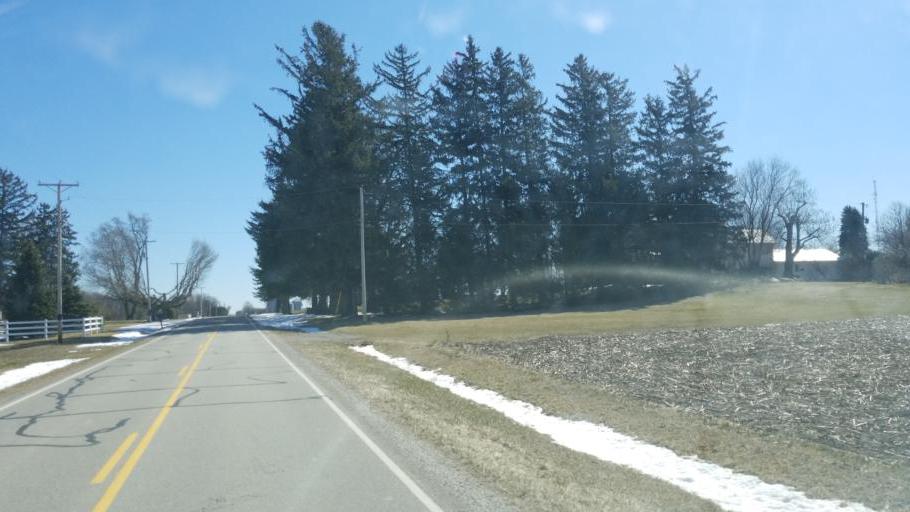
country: US
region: Ohio
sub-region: Crawford County
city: Bucyrus
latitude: 40.8048
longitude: -83.0587
